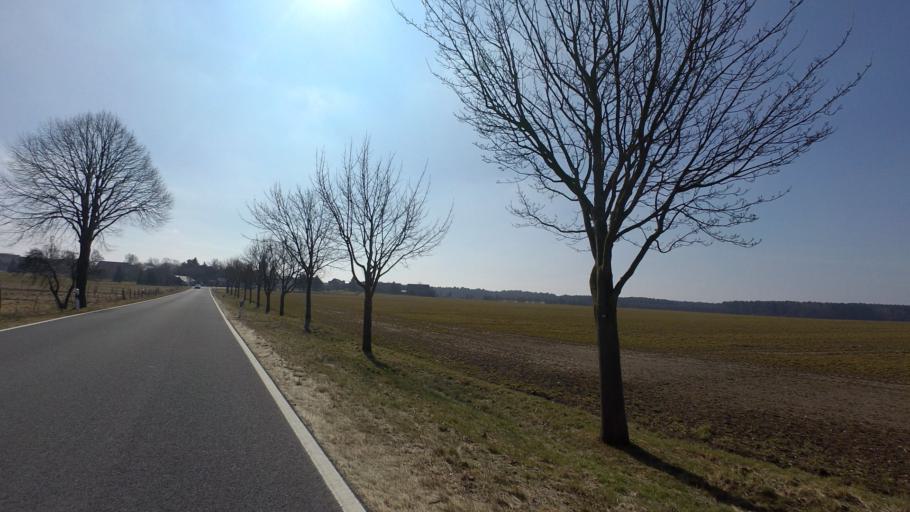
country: DE
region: Brandenburg
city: Wiesenburg
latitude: 52.0397
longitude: 12.5169
